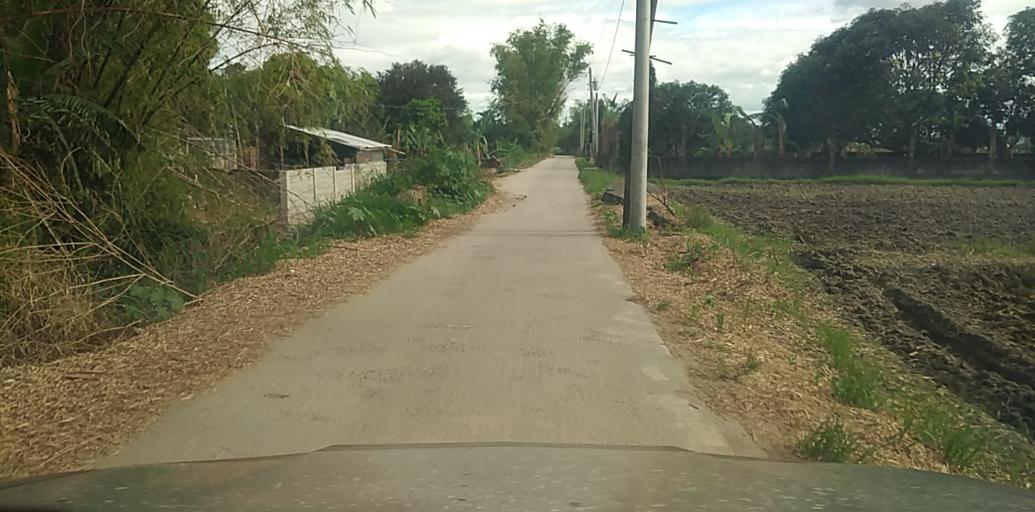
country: PH
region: Central Luzon
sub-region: Province of Pampanga
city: Panlinlang
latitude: 15.1841
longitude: 120.6963
